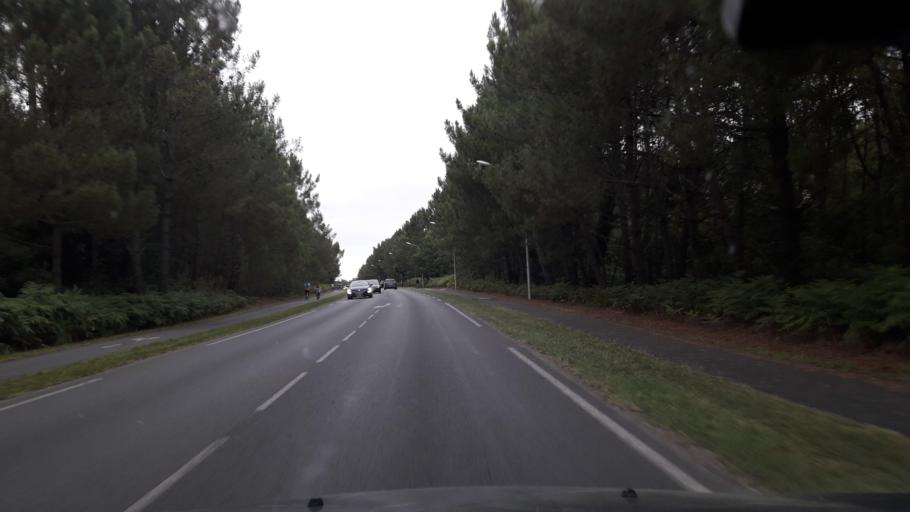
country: FR
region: Poitou-Charentes
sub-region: Departement de la Charente-Maritime
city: Les Mathes
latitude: 45.7074
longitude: -1.1624
